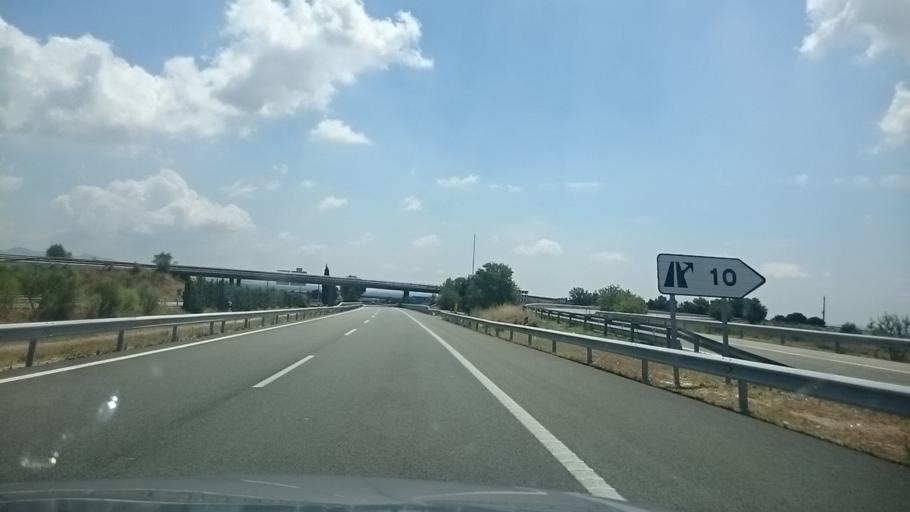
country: ES
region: Catalonia
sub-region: Provincia de Tarragona
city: El Pla de Santa Maria
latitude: 41.3693
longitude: 1.3007
